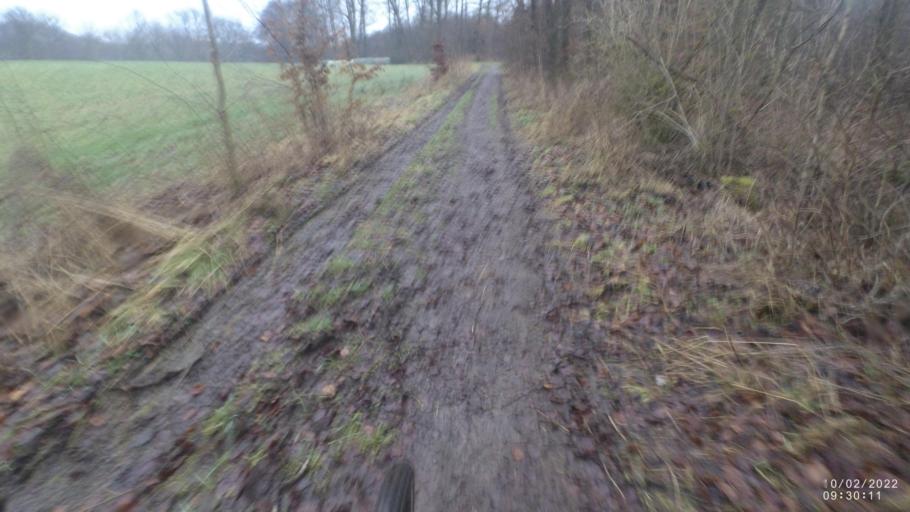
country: DE
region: North Rhine-Westphalia
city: Kierspe
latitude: 51.1805
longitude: 7.5790
